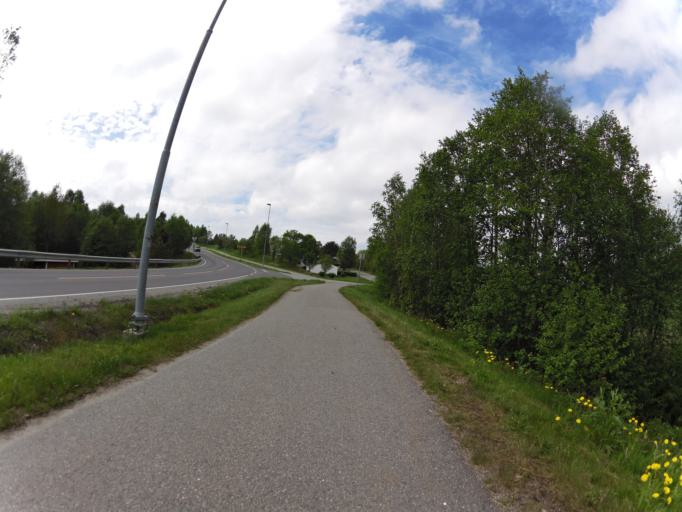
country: NO
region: Ostfold
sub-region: Rade
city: Karlshus
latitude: 59.3458
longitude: 10.9294
